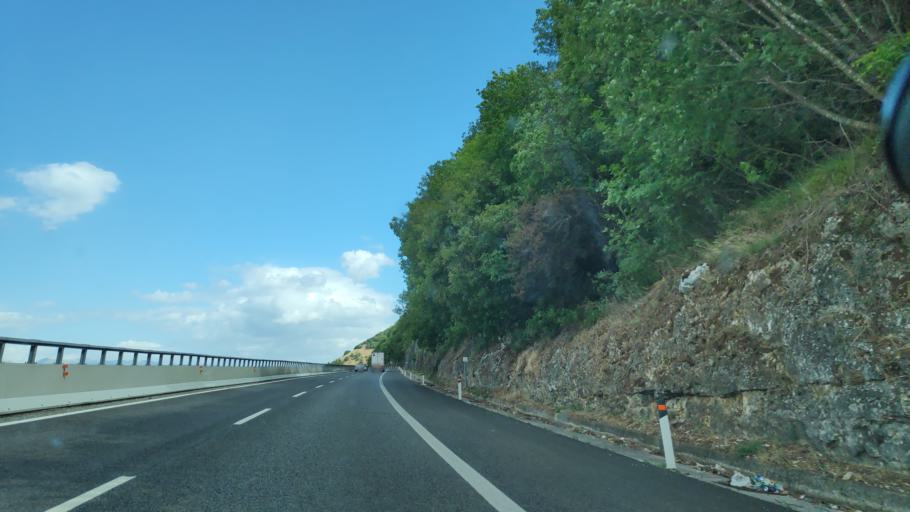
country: IT
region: Campania
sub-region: Provincia di Salerno
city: Sicignano degli Alburni
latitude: 40.5895
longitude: 15.3328
